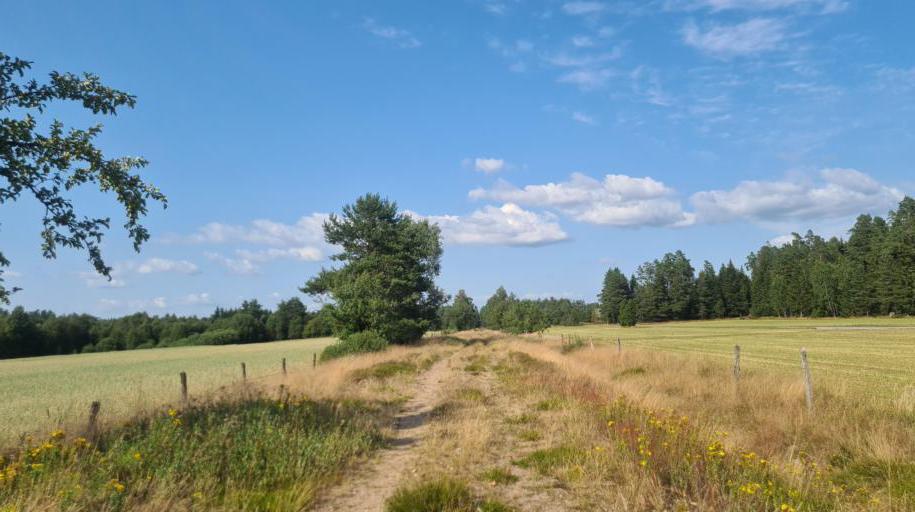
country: SE
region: Kronoberg
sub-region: Ljungby Kommun
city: Ljungby
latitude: 56.7569
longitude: 13.8875
